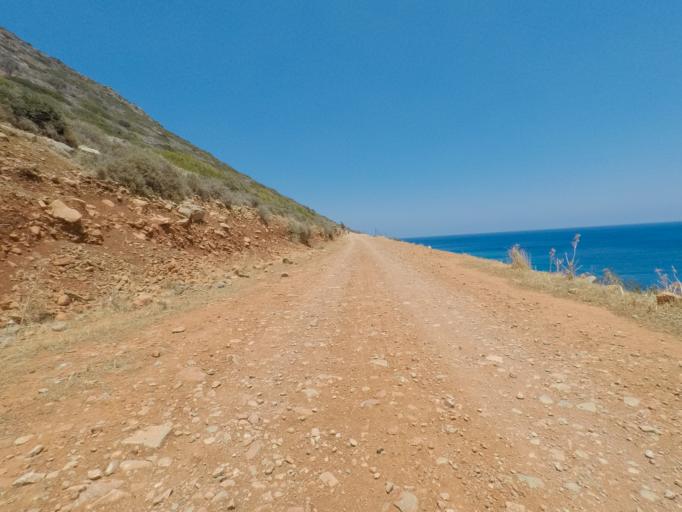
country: GR
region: Crete
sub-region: Nomos Lasithiou
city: Elounda
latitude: 35.3096
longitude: 25.7416
